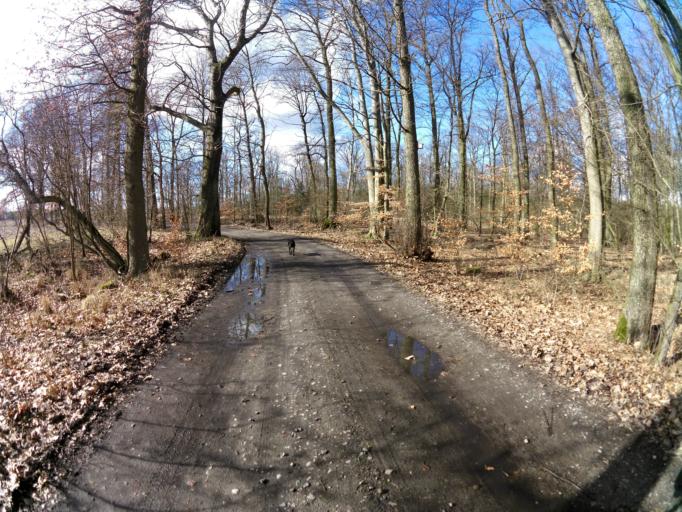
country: PL
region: West Pomeranian Voivodeship
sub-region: Powiat mysliborski
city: Debno
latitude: 52.7617
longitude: 14.7162
